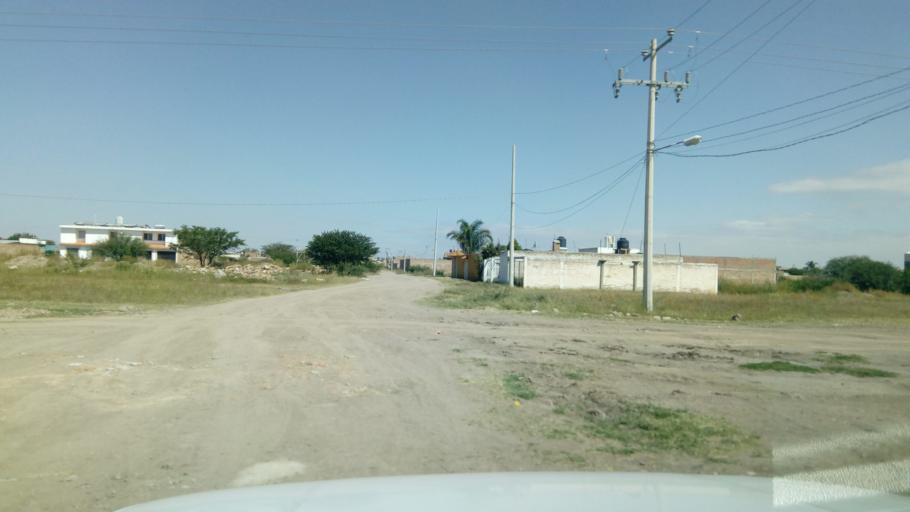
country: MX
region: Durango
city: Victoria de Durango
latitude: 23.9834
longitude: -104.6706
